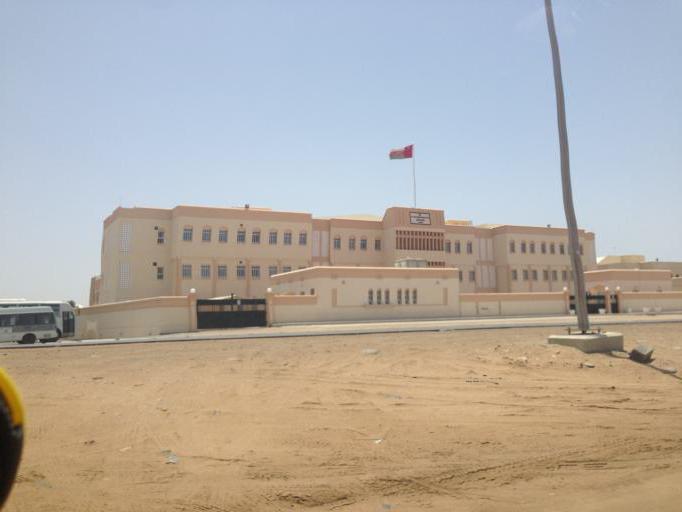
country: OM
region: Muhafazat Masqat
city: As Sib al Jadidah
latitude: 23.6302
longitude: 58.2523
